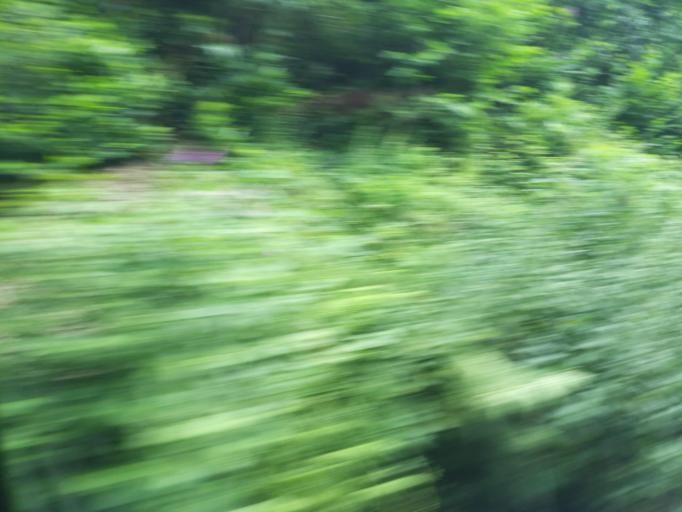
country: GB
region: England
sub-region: Cornwall
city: Par
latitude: 50.3687
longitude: -4.6835
